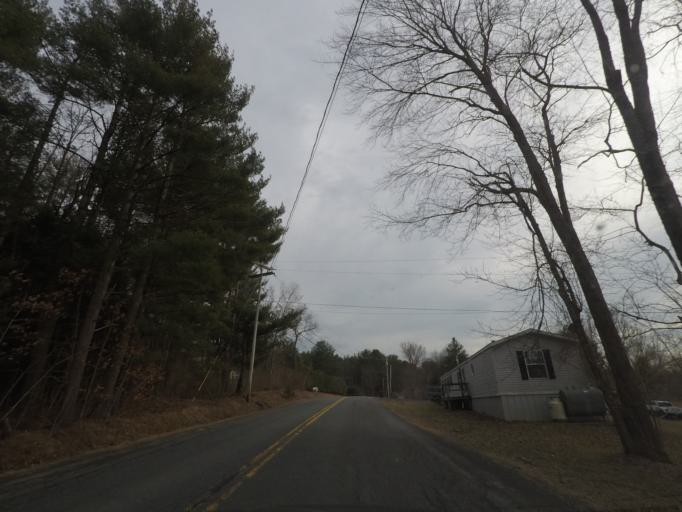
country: US
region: New York
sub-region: Rensselaer County
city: Hoosick Falls
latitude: 42.8492
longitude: -73.4555
